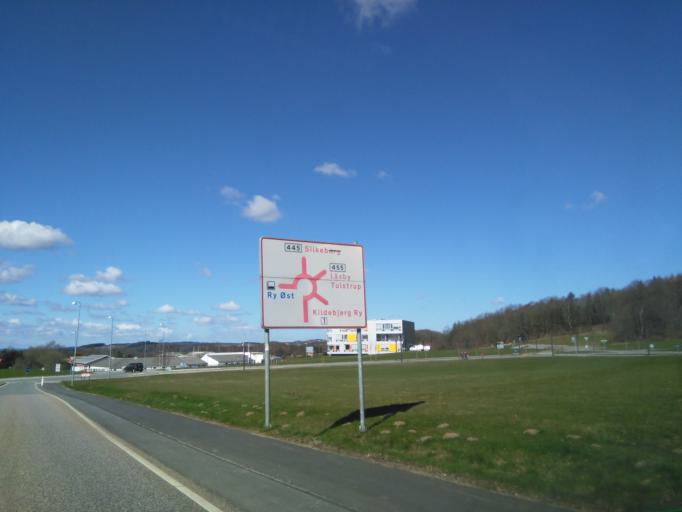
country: DK
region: Central Jutland
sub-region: Skanderborg Kommune
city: Ry
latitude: 56.0894
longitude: 9.7861
